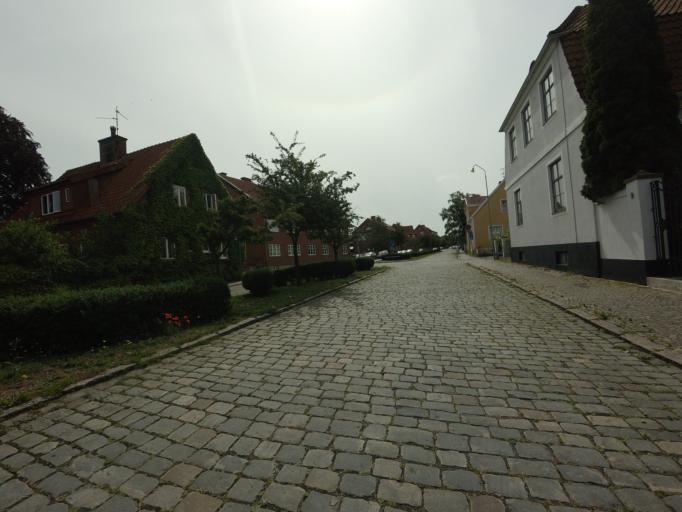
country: SE
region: Skane
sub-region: Simrishamns Kommun
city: Simrishamn
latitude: 55.5549
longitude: 14.3473
